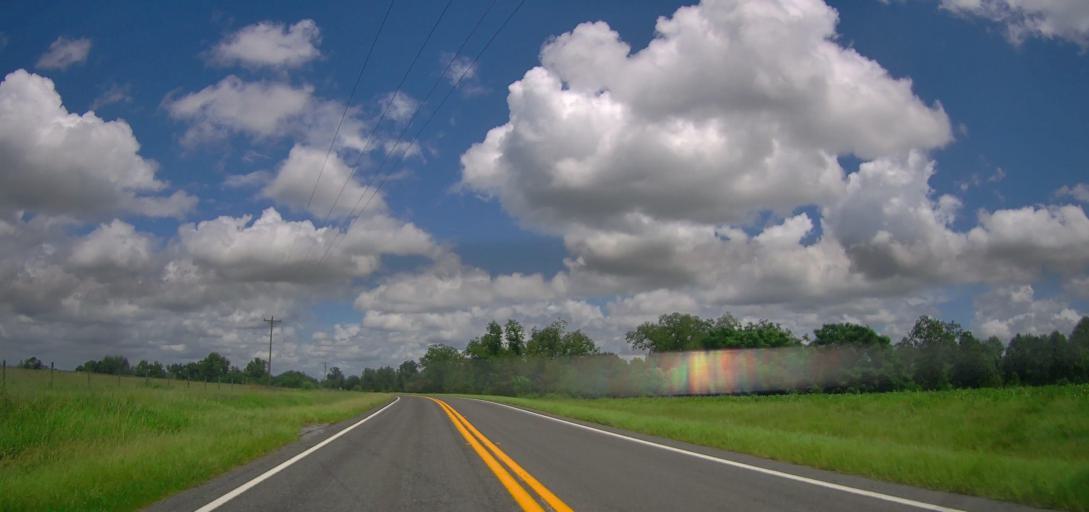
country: US
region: Georgia
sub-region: Turner County
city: Ashburn
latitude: 31.7974
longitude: -83.5819
